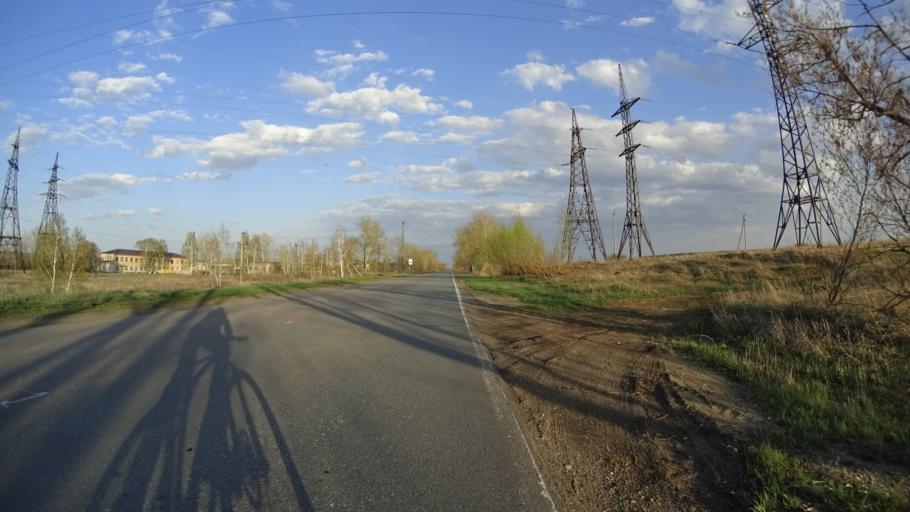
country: RU
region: Chelyabinsk
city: Troitsk
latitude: 54.0569
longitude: 61.5845
